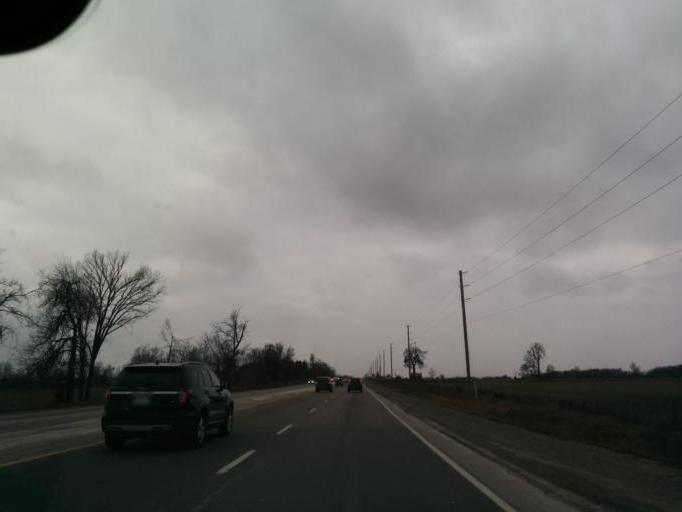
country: CA
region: Ontario
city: Brampton
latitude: 43.7545
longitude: -79.8526
